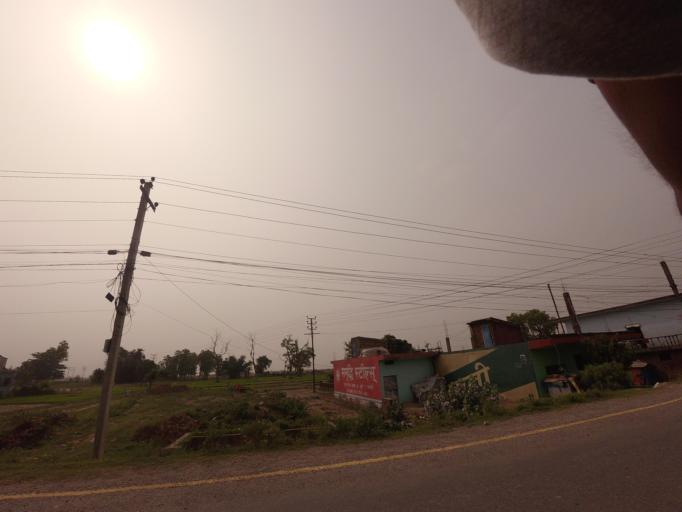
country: NP
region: Western Region
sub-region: Lumbini Zone
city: Bhairahawa
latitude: 27.5111
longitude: 83.3896
